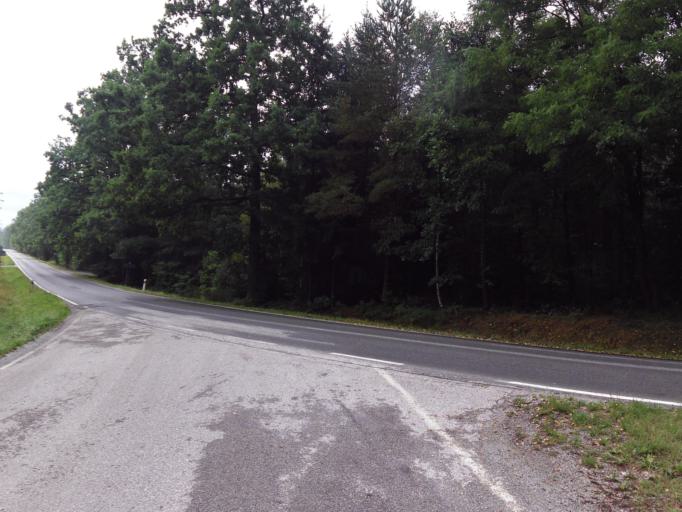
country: CZ
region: Jihocesky
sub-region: Okres Ceske Budejovice
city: Nove Hrady
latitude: 48.8383
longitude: 14.8054
